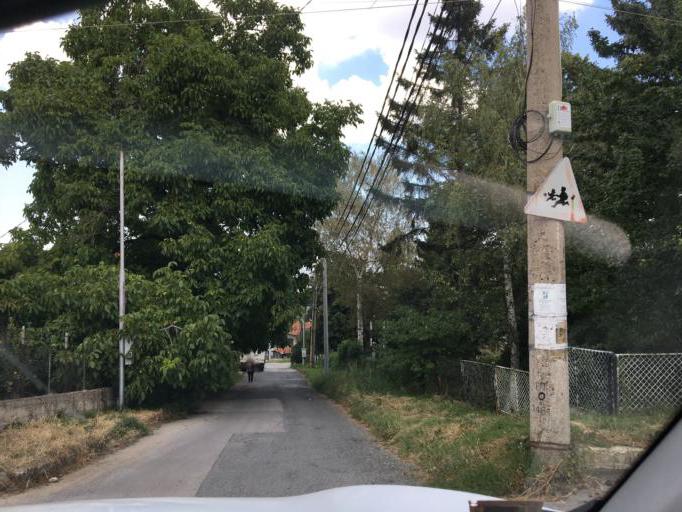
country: BG
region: Sofiya
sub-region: Obshtina Elin Pelin
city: Elin Pelin
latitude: 42.6001
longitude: 23.4734
